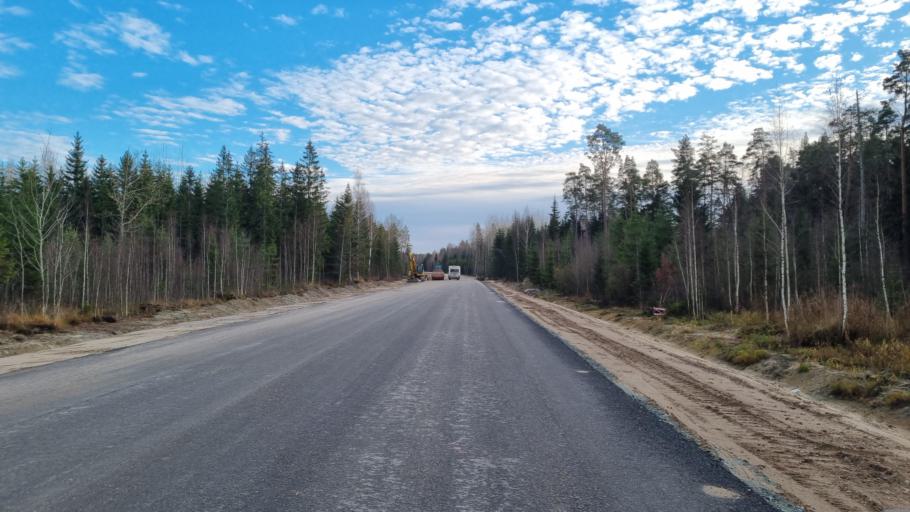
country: LV
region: Kekava
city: Kekava
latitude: 56.7957
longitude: 24.2097
